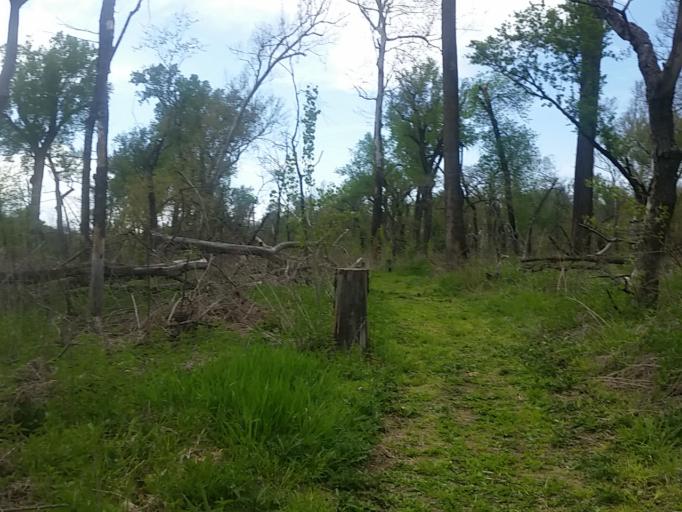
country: US
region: Nebraska
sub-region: Sarpy County
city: Bellevue
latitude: 41.1797
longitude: -95.8972
